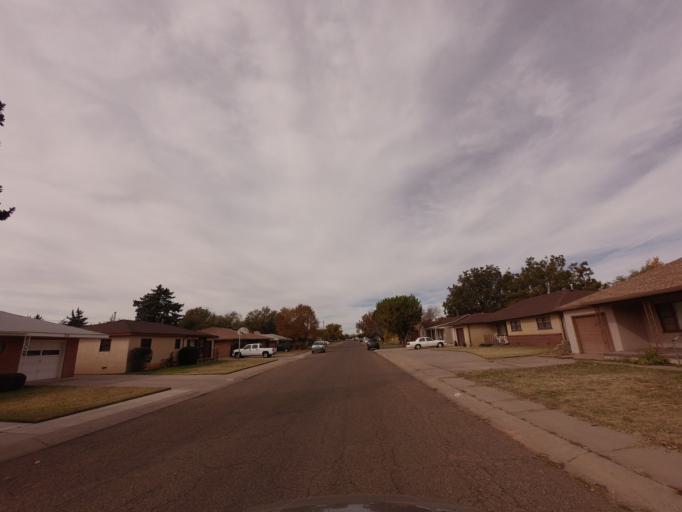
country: US
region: New Mexico
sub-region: Curry County
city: Clovis
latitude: 34.4254
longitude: -103.2103
